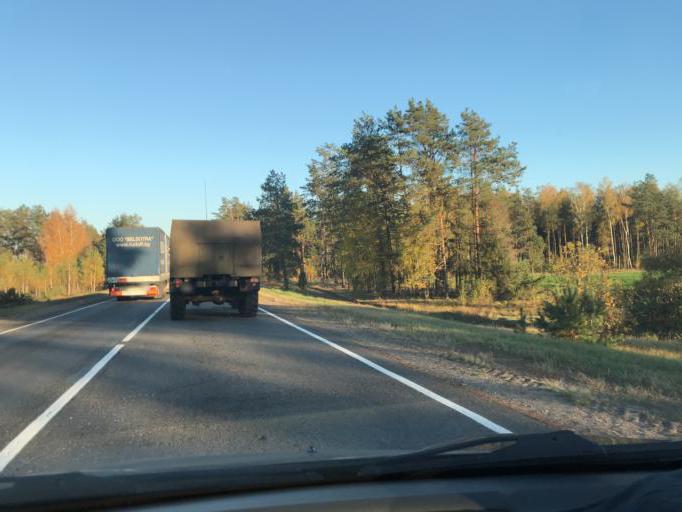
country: BY
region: Minsk
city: Staryya Darohi
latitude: 53.0480
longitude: 28.0852
